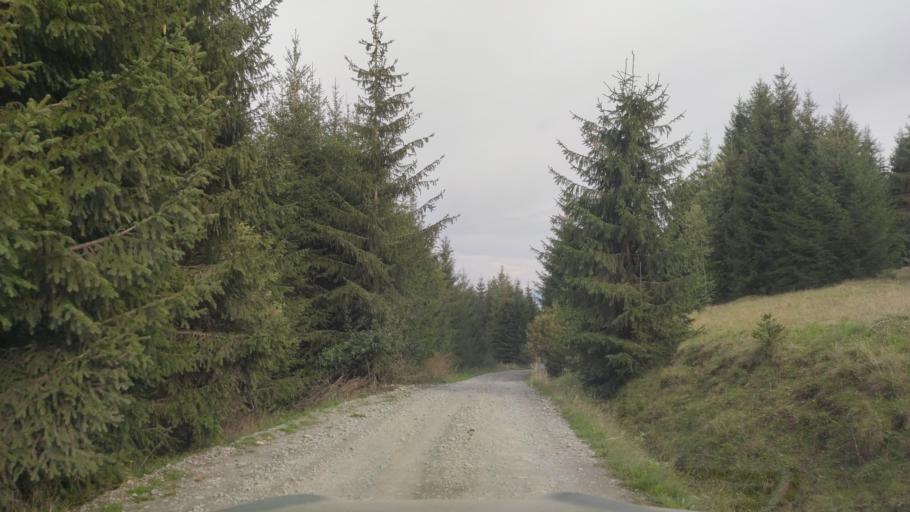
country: RO
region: Harghita
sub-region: Comuna Remetea
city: Remetea
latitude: 46.8140
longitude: 25.3566
